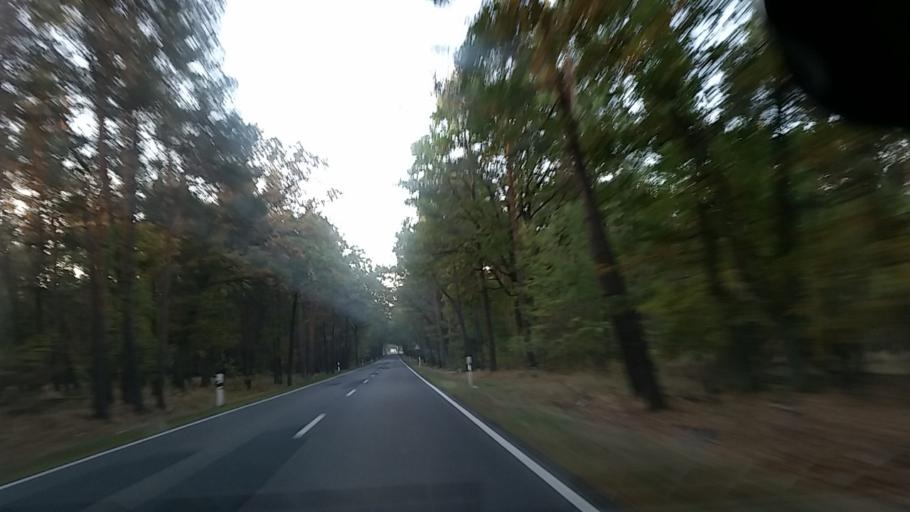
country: DE
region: Lower Saxony
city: Luder
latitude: 52.7809
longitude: 10.7152
